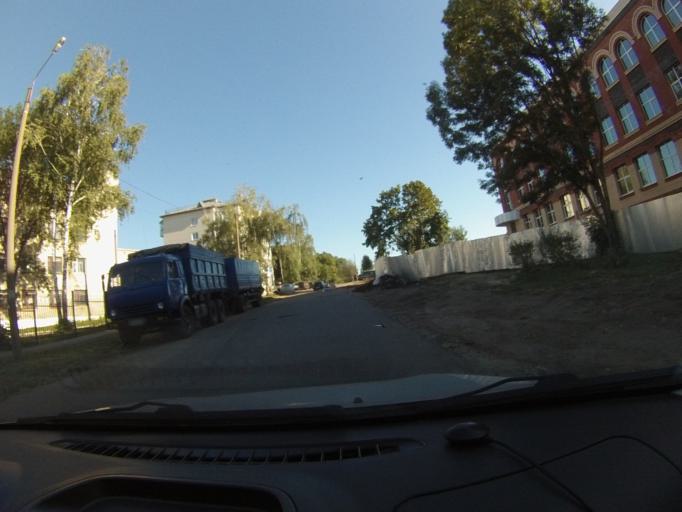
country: RU
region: Tambov
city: Tambov
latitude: 52.7537
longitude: 41.4274
